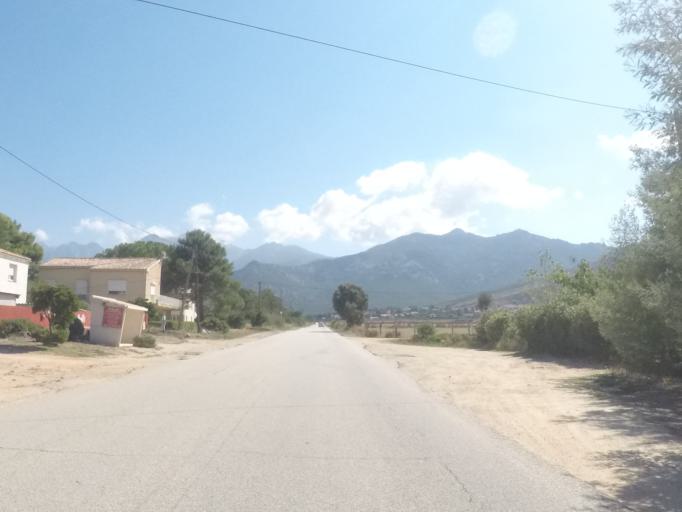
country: FR
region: Corsica
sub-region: Departement de la Haute-Corse
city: Calenzana
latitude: 42.4997
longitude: 8.7930
